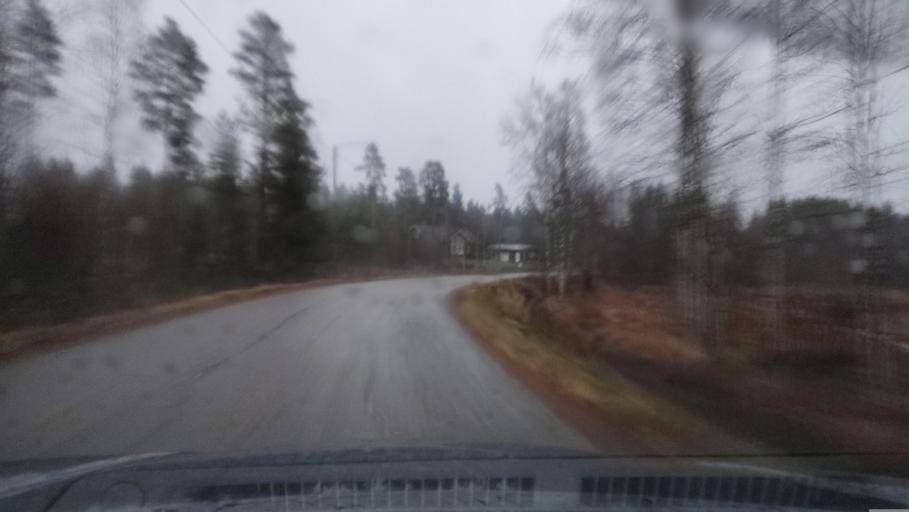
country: FI
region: Southern Ostrobothnia
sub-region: Suupohja
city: Karijoki
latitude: 62.1447
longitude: 21.5664
